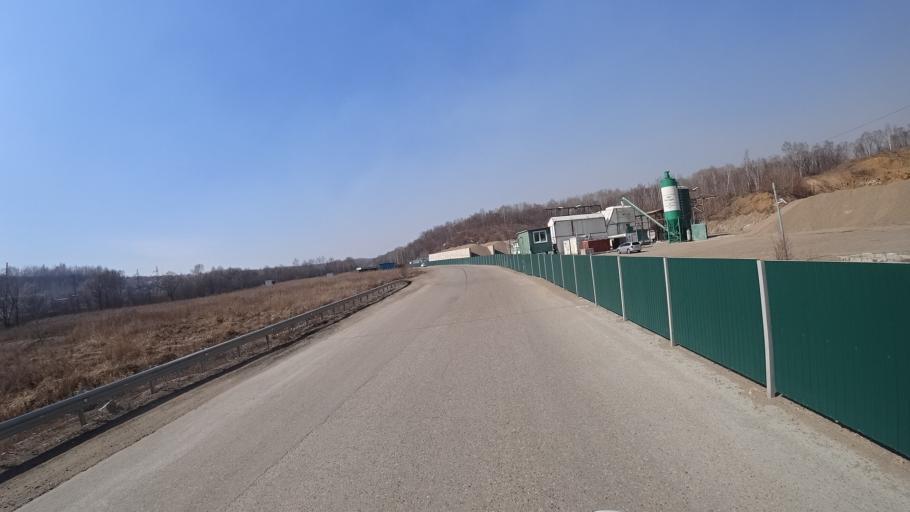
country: RU
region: Amur
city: Novobureyskiy
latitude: 49.7932
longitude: 129.9632
